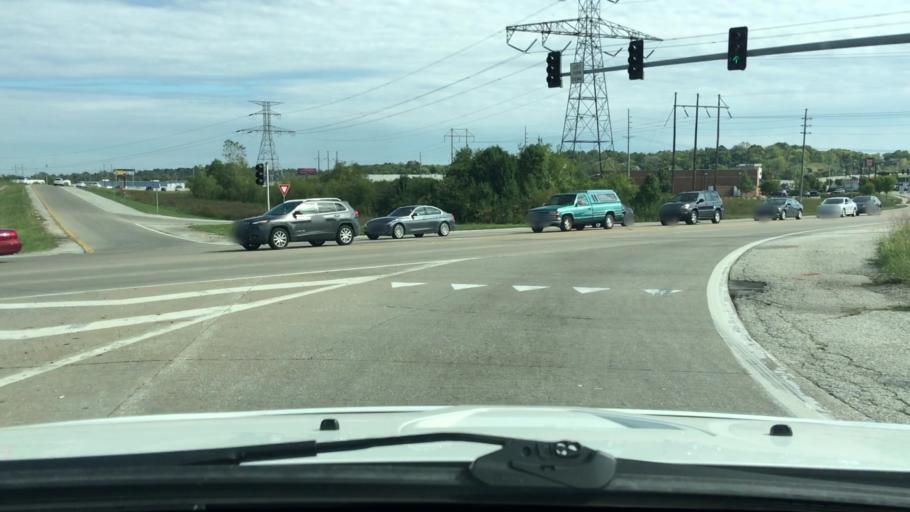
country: US
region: Missouri
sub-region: Saint Charles County
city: Saint Charles
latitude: 38.8235
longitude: -90.5181
